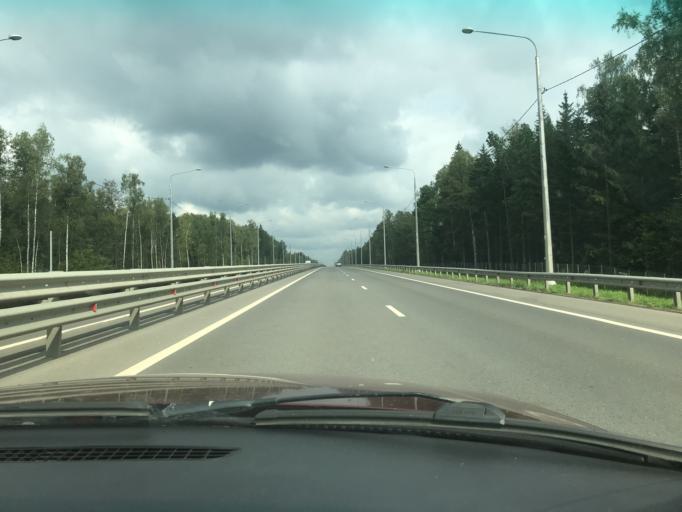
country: RU
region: Kaluga
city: Pyatovskiy
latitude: 54.6540
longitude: 36.1390
